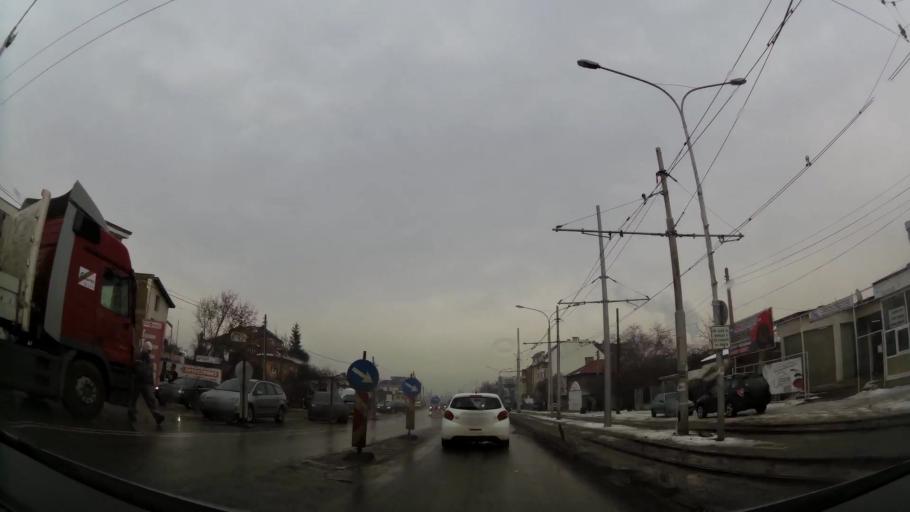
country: BG
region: Sofia-Capital
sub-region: Stolichna Obshtina
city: Sofia
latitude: 42.6828
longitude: 23.2717
